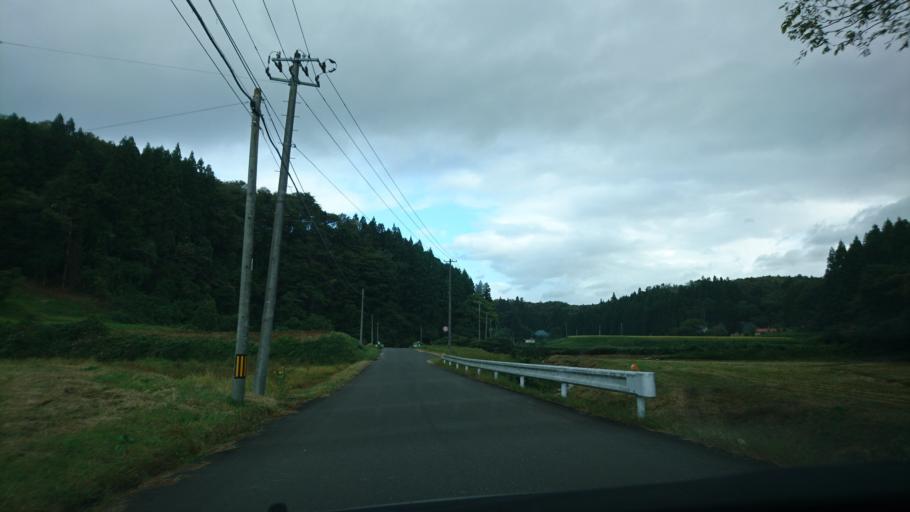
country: JP
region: Iwate
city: Ichinoseki
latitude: 38.9042
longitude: 141.0816
